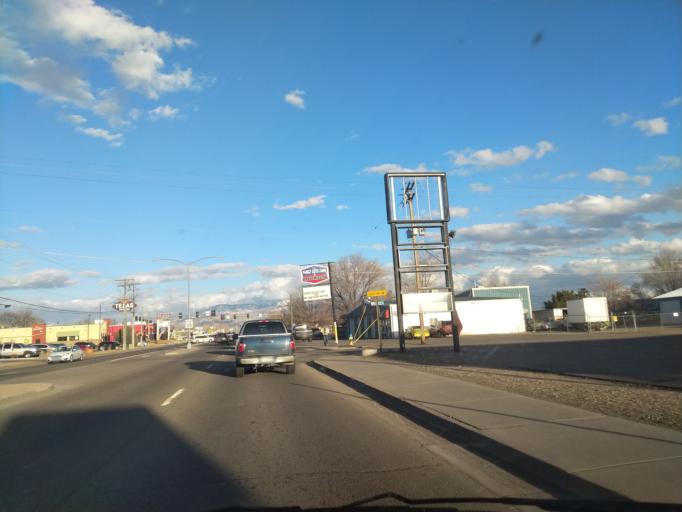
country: US
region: Colorado
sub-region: Mesa County
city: Fruitvale
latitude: 39.0773
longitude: -108.5214
